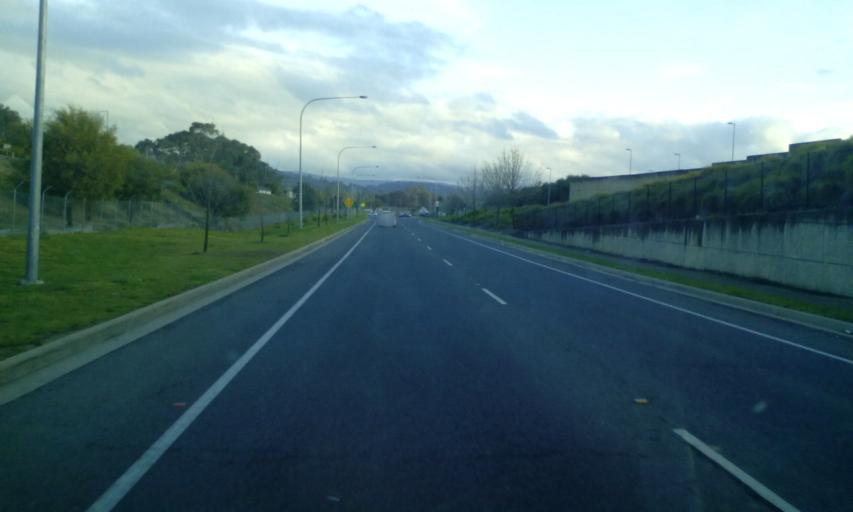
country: AU
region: New South Wales
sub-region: Albury Municipality
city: East Albury
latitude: -36.0879
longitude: 146.9234
